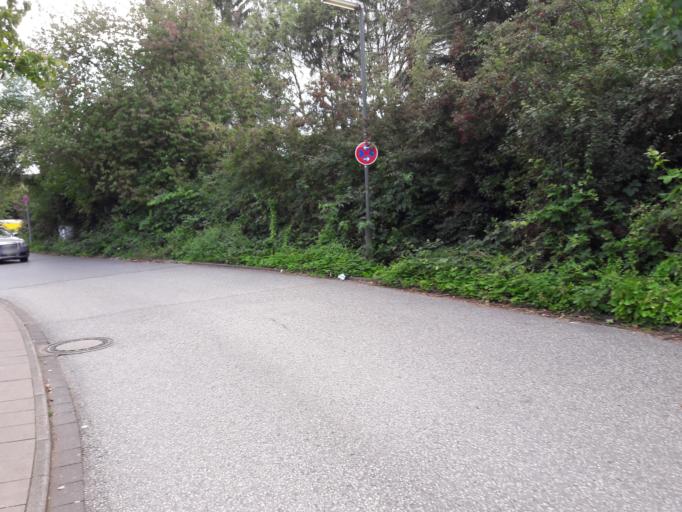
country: DE
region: North Rhine-Westphalia
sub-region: Regierungsbezirk Dusseldorf
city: Dusseldorf
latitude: 51.2032
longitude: 6.8373
